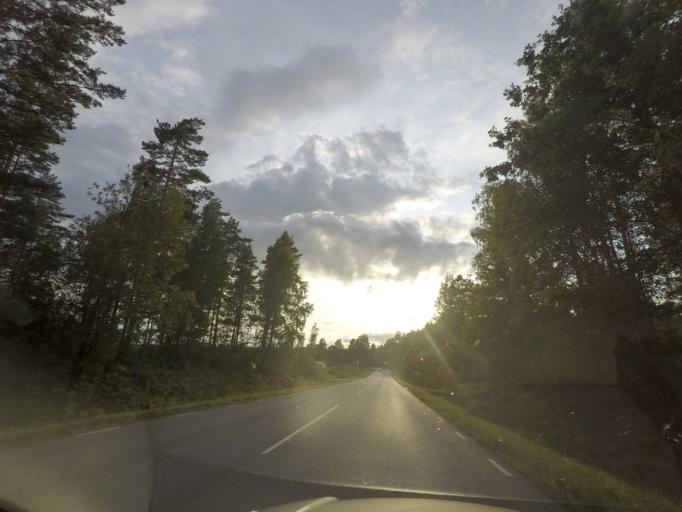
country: SE
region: OErebro
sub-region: Lindesbergs Kommun
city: Frovi
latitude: 59.4618
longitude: 15.3914
